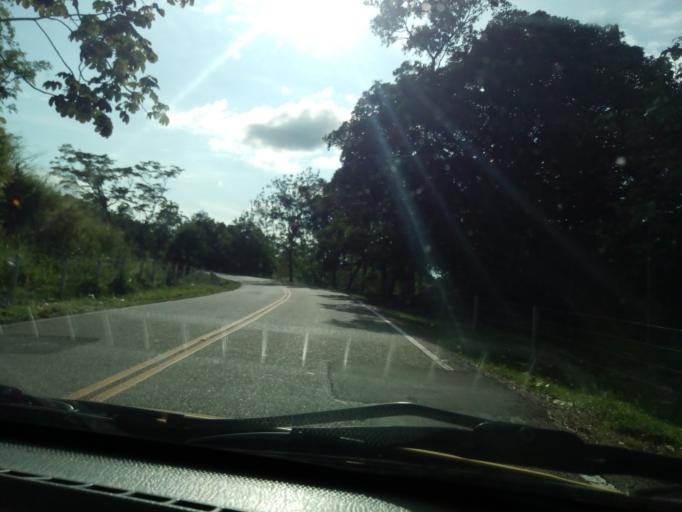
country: CO
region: Boyaca
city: Puerto Boyaca
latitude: 5.9547
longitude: -74.4867
